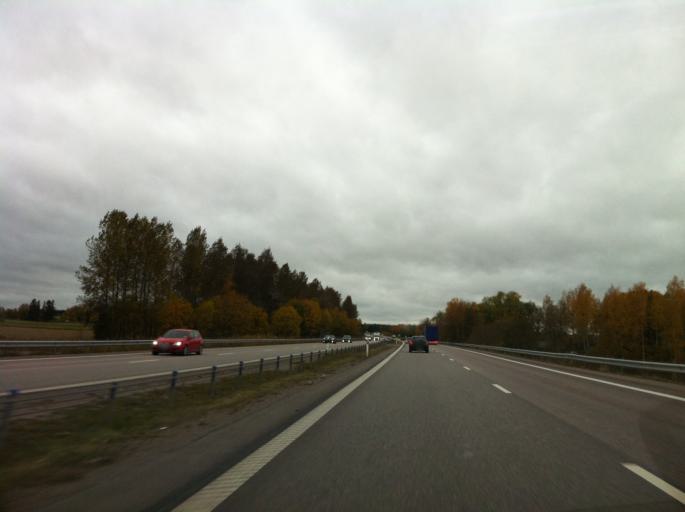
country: SE
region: OEstergoetland
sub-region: Mjolby Kommun
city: Mantorp
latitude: 58.3560
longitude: 15.2211
